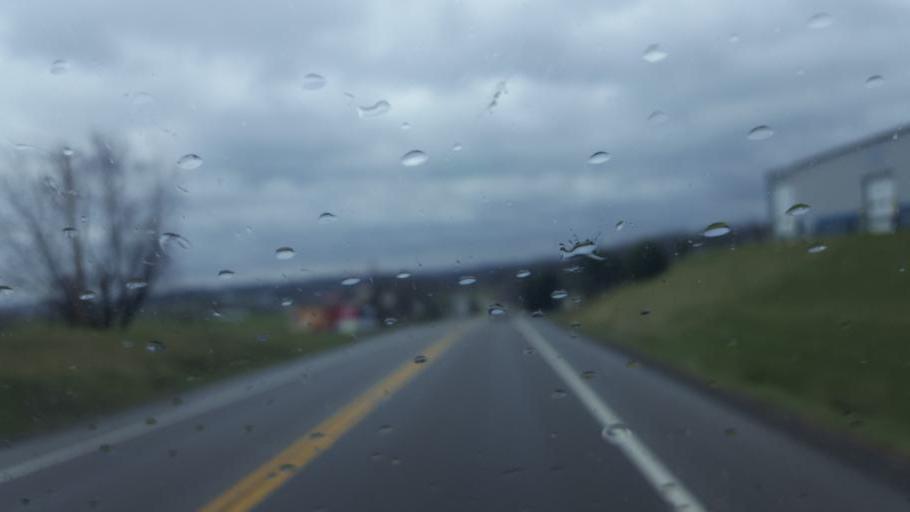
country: US
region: Ohio
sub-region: Holmes County
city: Millersburg
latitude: 40.5529
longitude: -81.8417
